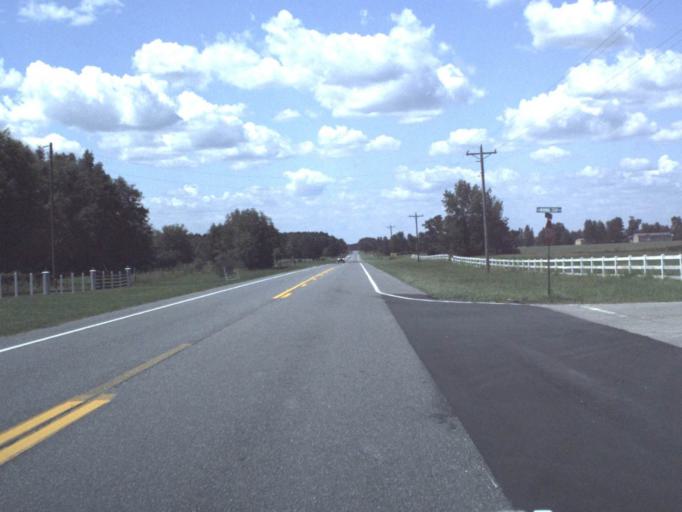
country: US
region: Florida
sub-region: Columbia County
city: Lake City
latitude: 30.0034
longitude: -82.7101
